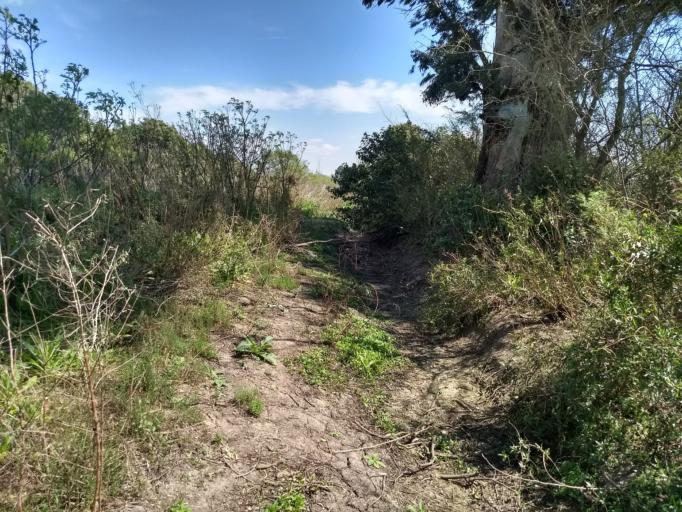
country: AR
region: Santa Fe
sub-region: Departamento de San Lorenzo
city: San Lorenzo
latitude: -32.7047
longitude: -60.7772
